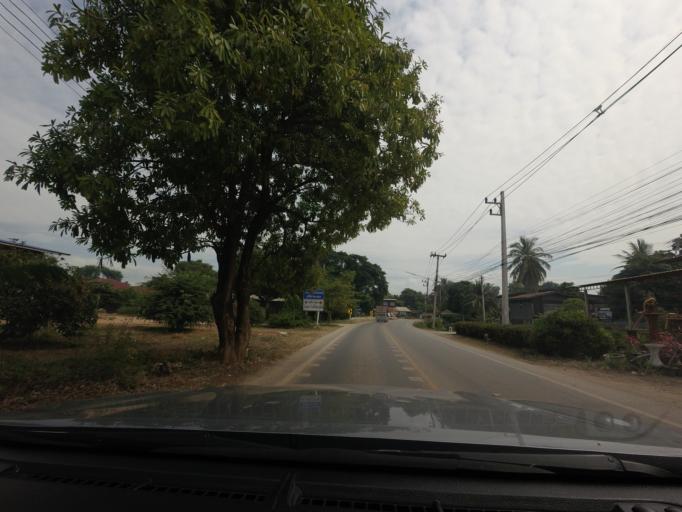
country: TH
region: Phitsanulok
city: Phitsanulok
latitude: 16.7249
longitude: 100.3159
